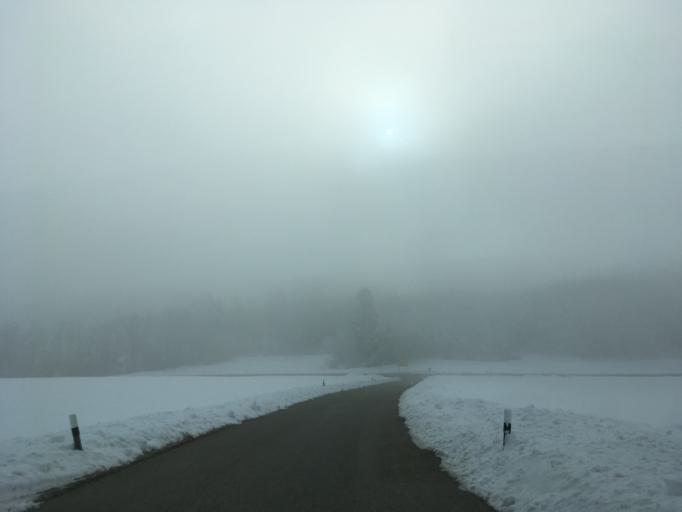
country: DE
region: Bavaria
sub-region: Upper Bavaria
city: Rimsting
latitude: 47.8597
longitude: 12.2957
